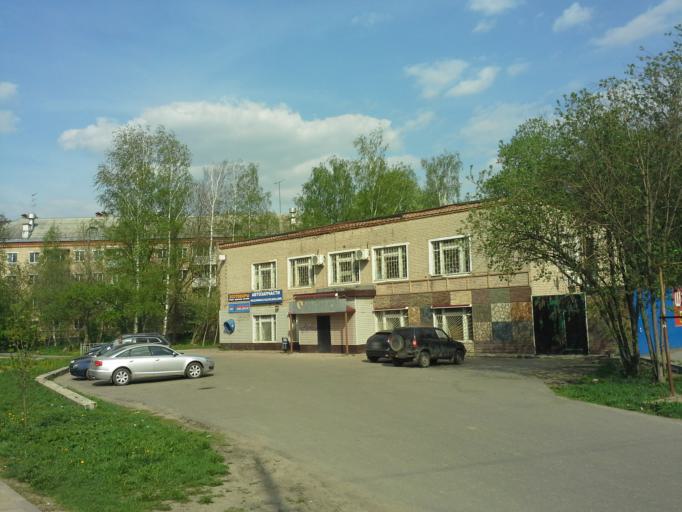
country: RU
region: Moskovskaya
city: Sergiyev Posad
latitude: 56.3207
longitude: 38.1429
